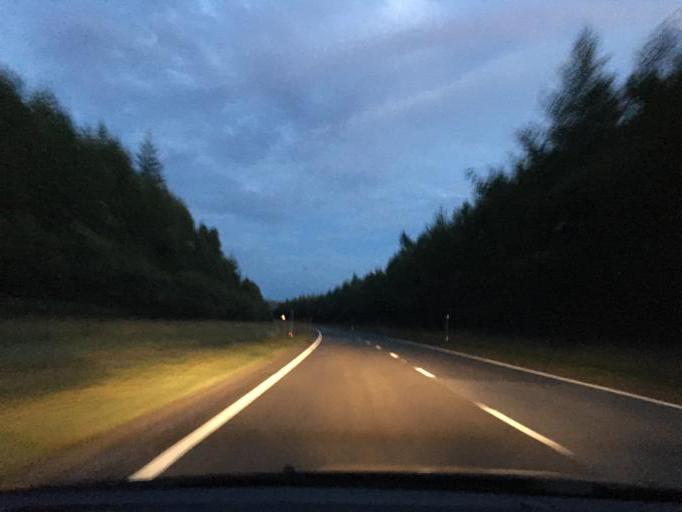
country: GB
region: Scotland
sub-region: Perth and Kinross
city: Aberfeldy
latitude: 56.7742
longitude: -3.9809
